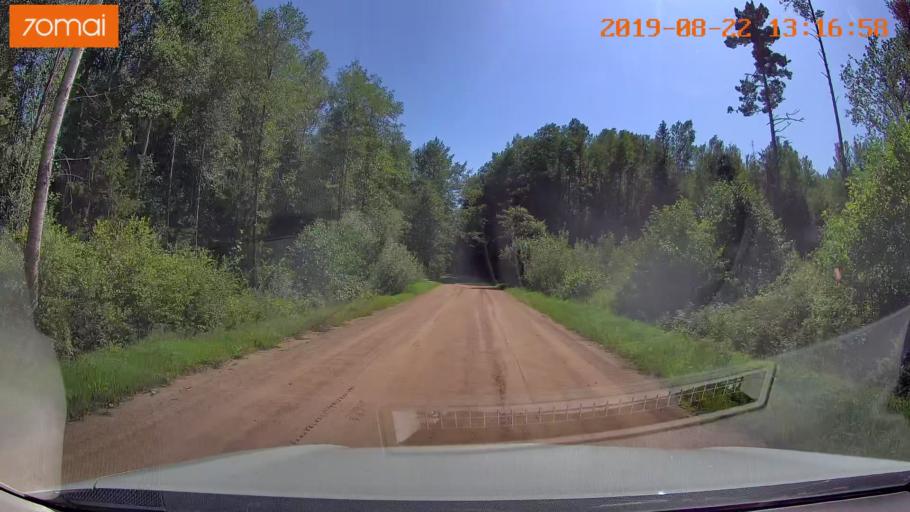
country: BY
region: Minsk
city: Prawdzinski
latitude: 53.2517
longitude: 27.9165
